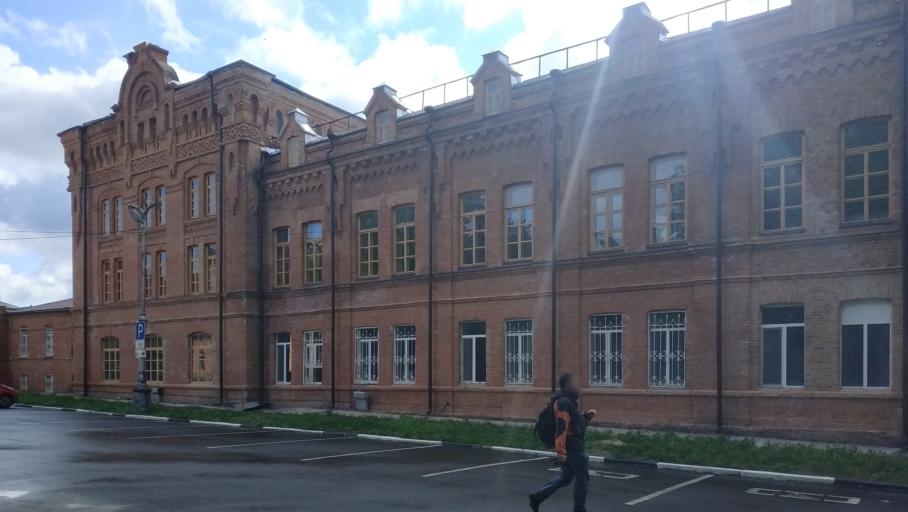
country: RU
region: Brjansk
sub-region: Bryanskiy Rayon
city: Bryansk
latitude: 53.2423
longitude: 34.3672
